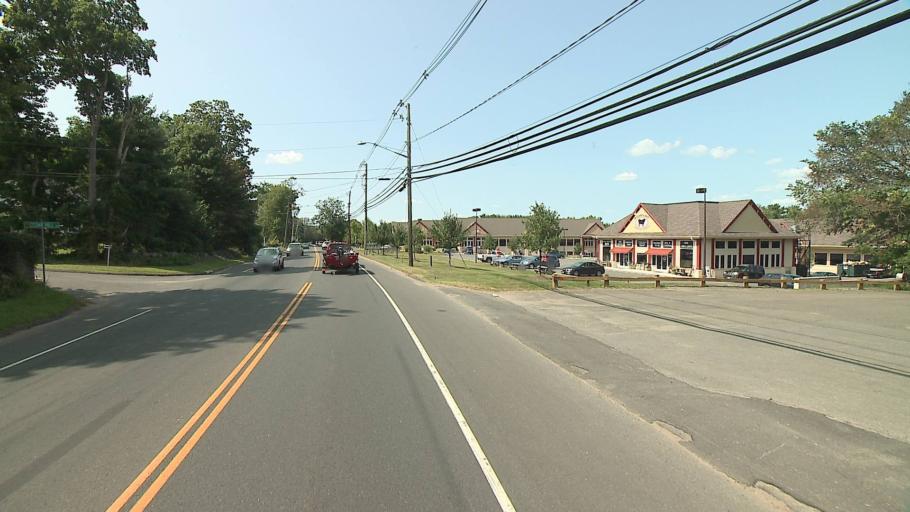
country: US
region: Connecticut
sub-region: Fairfield County
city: Newtown
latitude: 41.3883
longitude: -73.2865
